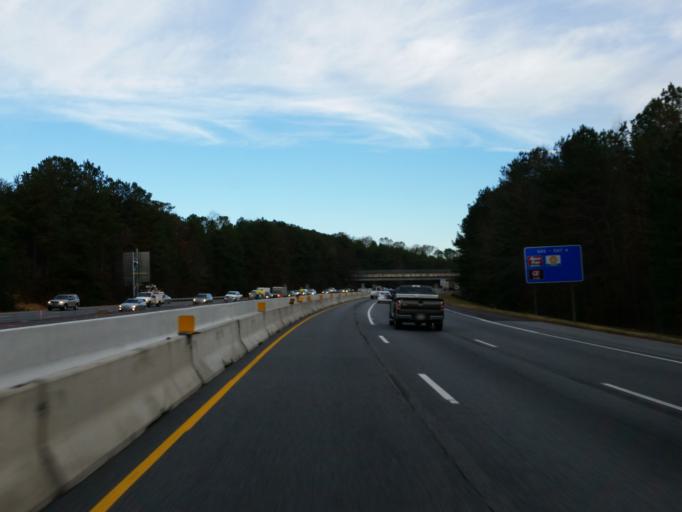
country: US
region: Georgia
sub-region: Cobb County
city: Kennesaw
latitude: 34.0447
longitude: -84.5634
